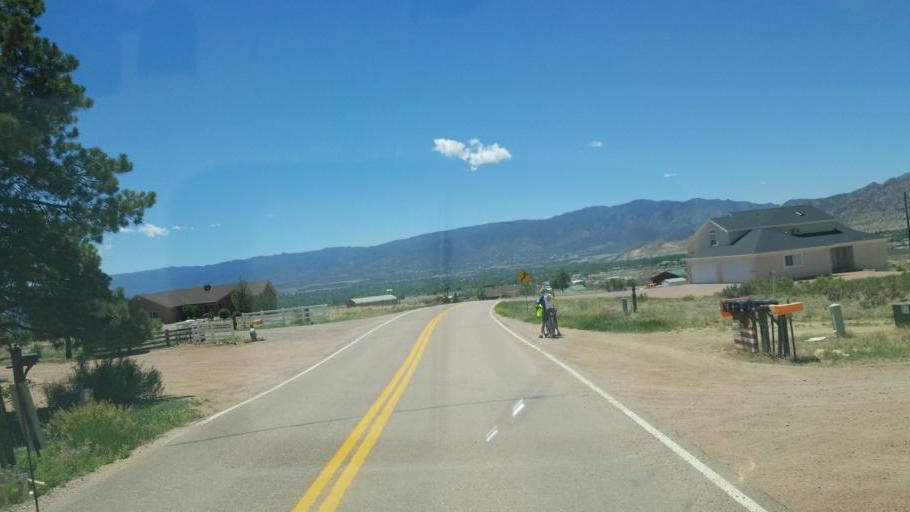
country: US
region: Colorado
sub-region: Fremont County
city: Canon City
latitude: 38.4858
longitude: -105.2141
